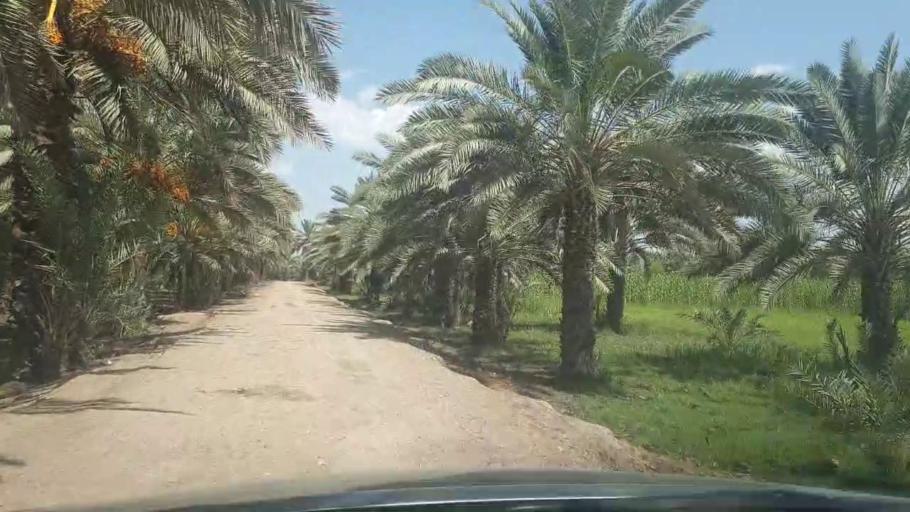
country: PK
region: Sindh
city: Khairpur
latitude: 27.5486
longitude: 68.8006
